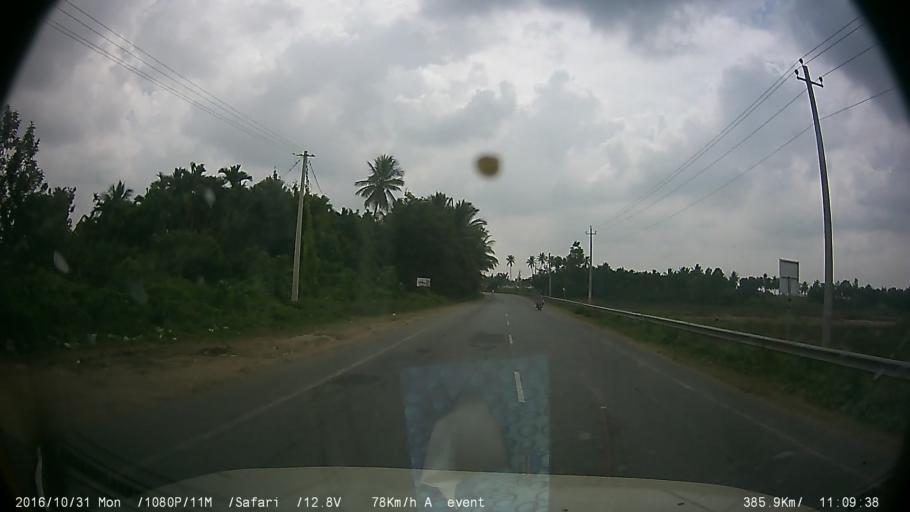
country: IN
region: Karnataka
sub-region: Mysore
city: Piriyapatna
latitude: 12.3514
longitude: 76.0688
